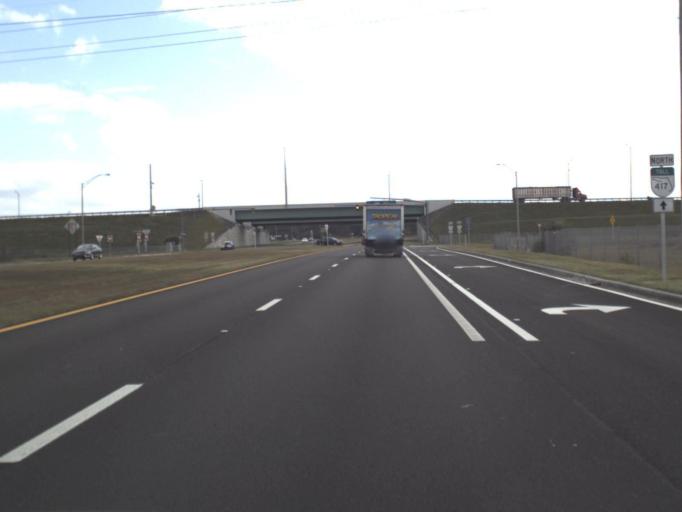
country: US
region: Florida
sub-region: Osceola County
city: Celebration
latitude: 28.3429
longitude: -81.5195
